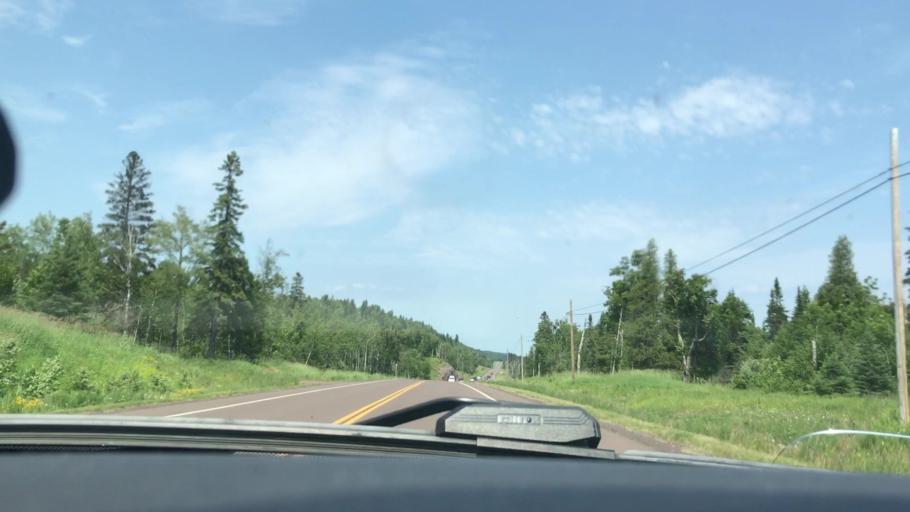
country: US
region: Minnesota
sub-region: Lake County
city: Silver Bay
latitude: 47.4320
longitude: -91.0849
